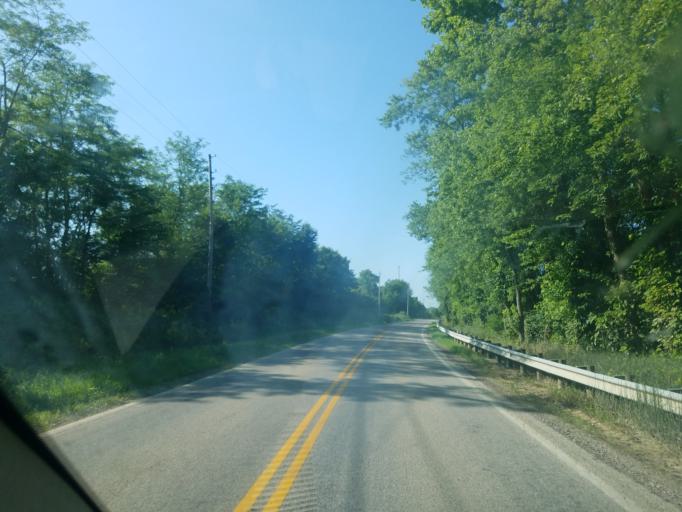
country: US
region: Ohio
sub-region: Marion County
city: Prospect
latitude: 40.4760
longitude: -83.1888
